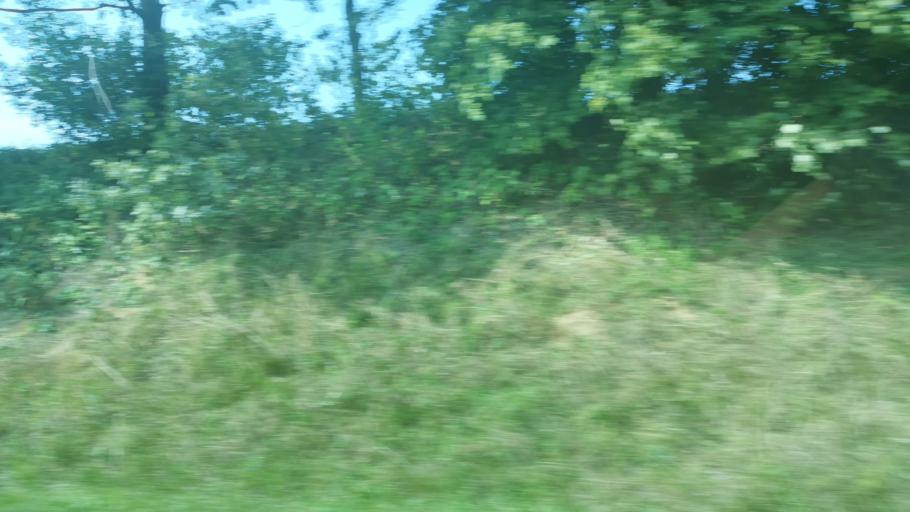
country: DE
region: Bavaria
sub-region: Upper Palatinate
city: Pemfling
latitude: 49.2642
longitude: 12.6318
